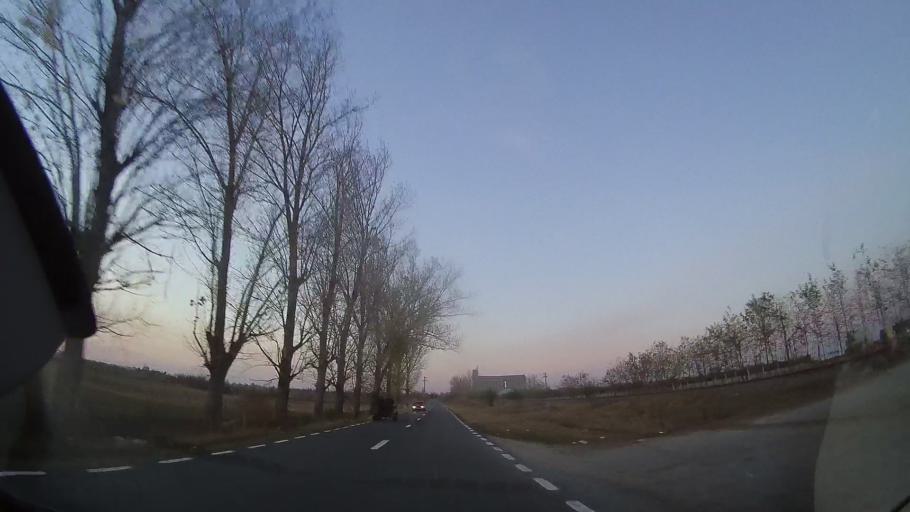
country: RO
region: Constanta
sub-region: Comuna Cobadin
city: Cobadin
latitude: 44.0471
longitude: 28.2517
